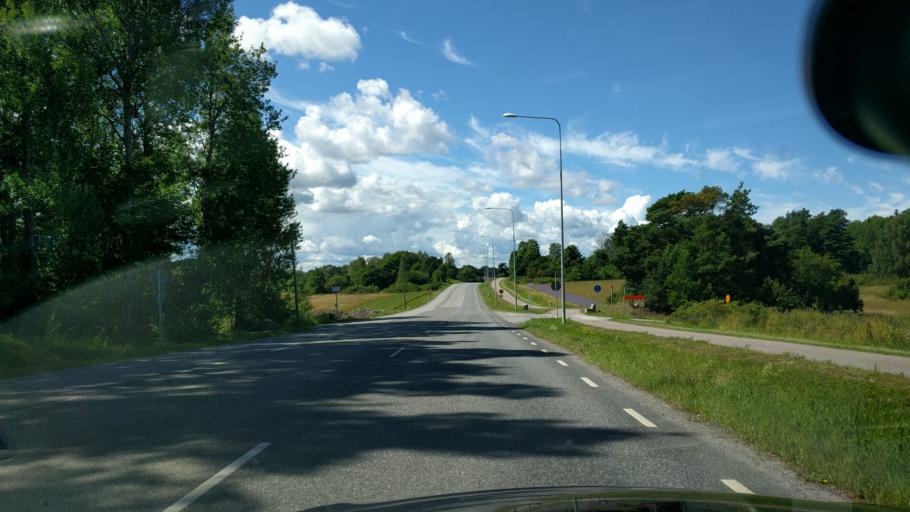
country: SE
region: Stockholm
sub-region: Jarfalla Kommun
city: Jakobsberg
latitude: 59.4092
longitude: 17.8832
